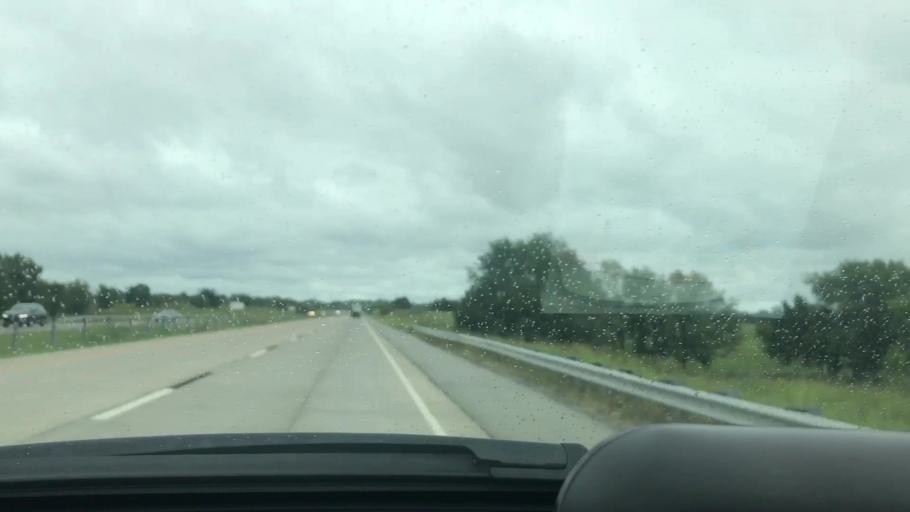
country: US
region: Oklahoma
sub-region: Pittsburg County
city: McAlester
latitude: 34.8133
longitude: -95.8577
